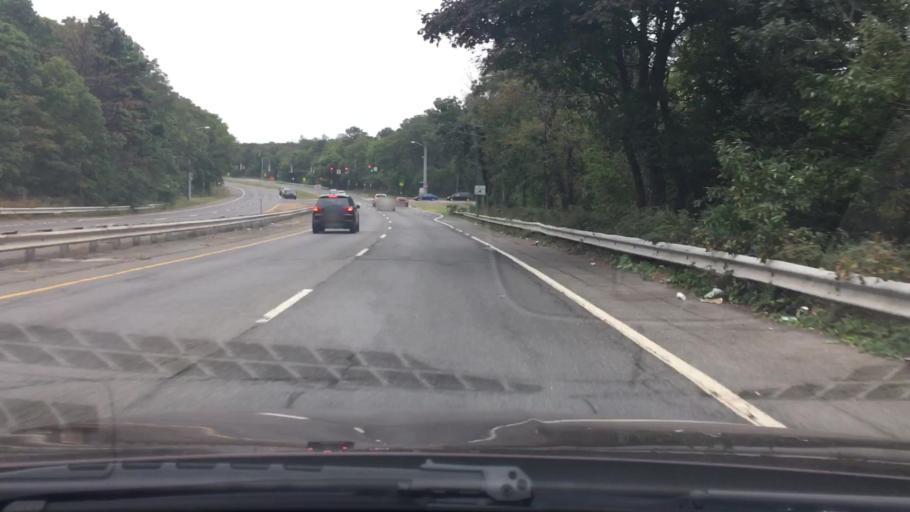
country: US
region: New York
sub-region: Suffolk County
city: Islandia
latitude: 40.7943
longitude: -73.1691
